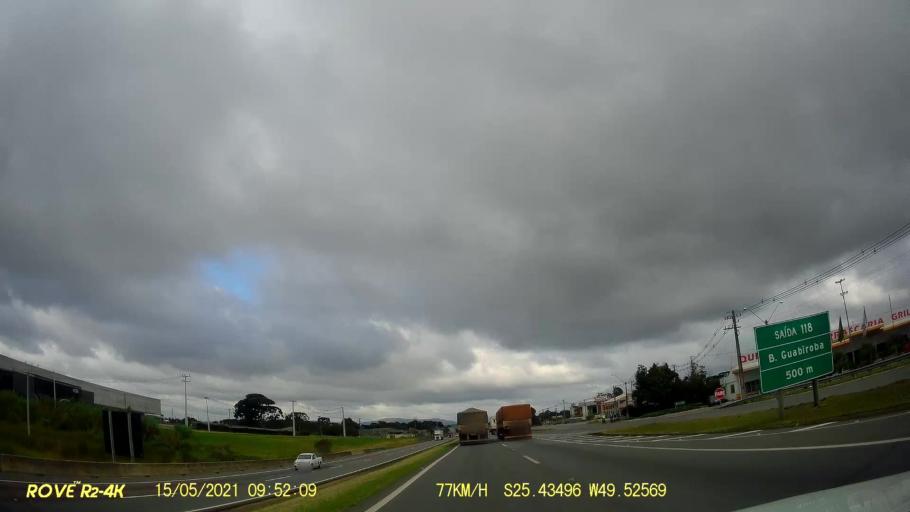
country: BR
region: Parana
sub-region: Campo Largo
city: Campo Largo
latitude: -25.4346
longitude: -49.5252
